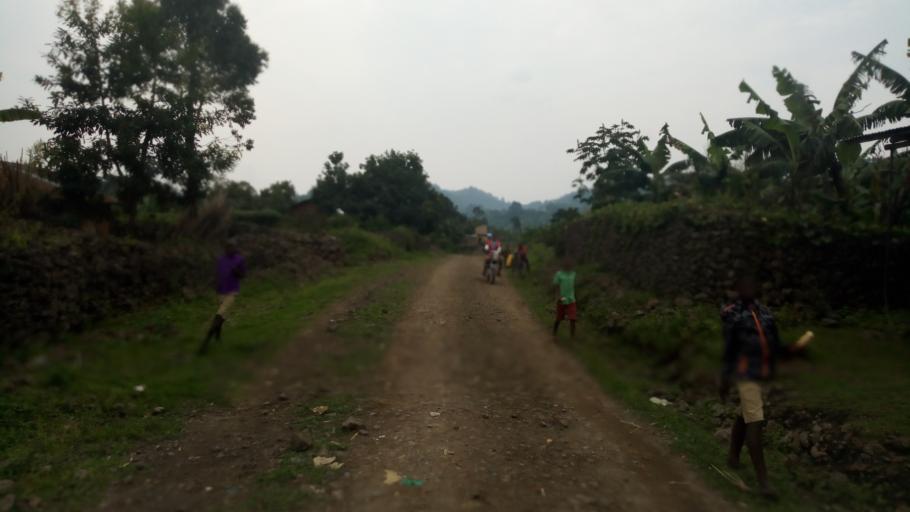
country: UG
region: Western Region
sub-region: Kisoro District
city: Kisoro
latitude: -1.2656
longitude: 29.6262
